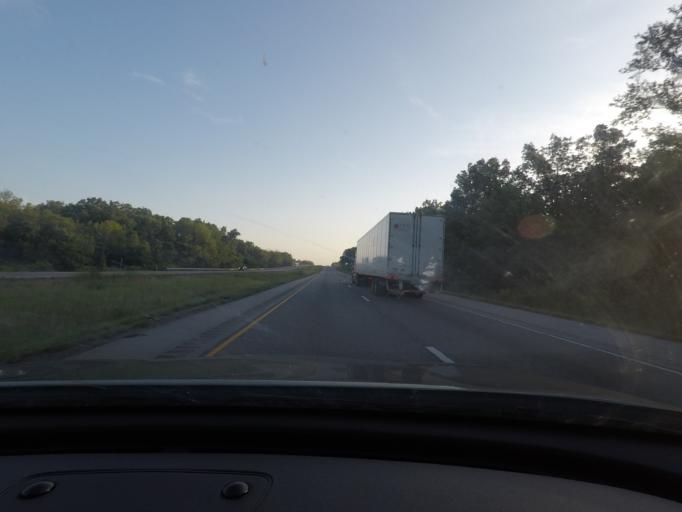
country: US
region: Illinois
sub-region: Williamson County
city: Johnston City
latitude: 37.8459
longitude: -88.9437
